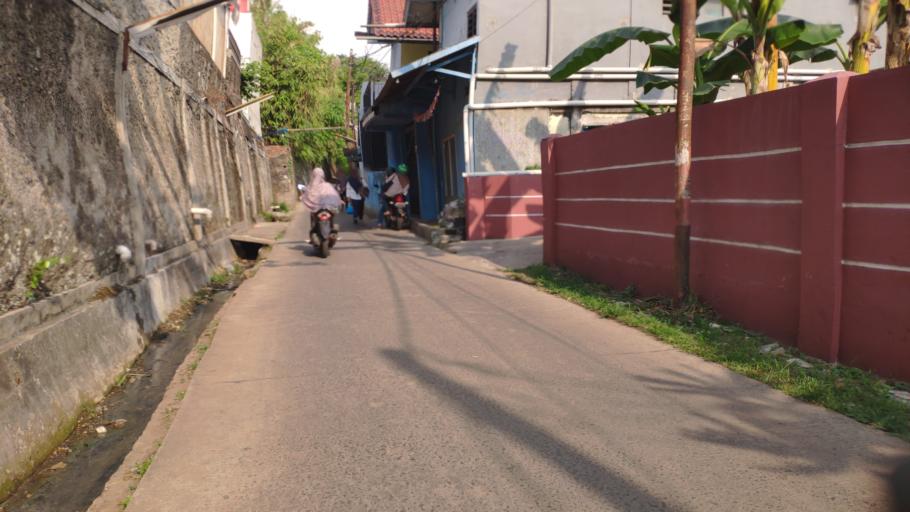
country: ID
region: West Java
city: Pamulang
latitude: -6.3171
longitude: 106.7943
